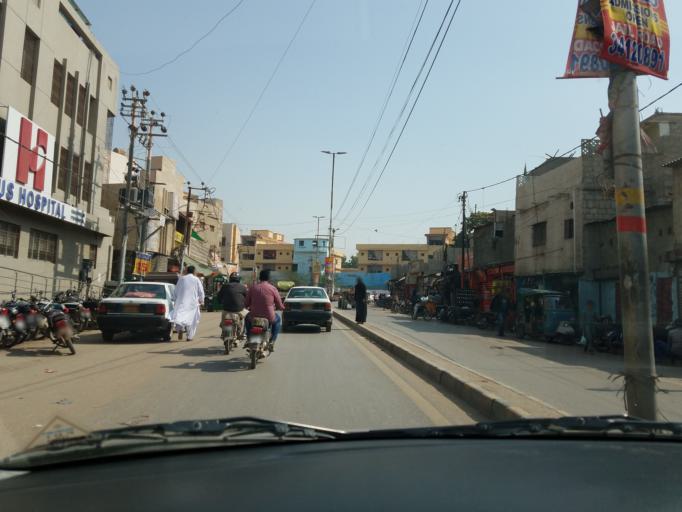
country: PK
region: Sindh
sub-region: Karachi District
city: Karachi
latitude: 24.8906
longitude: 67.0513
